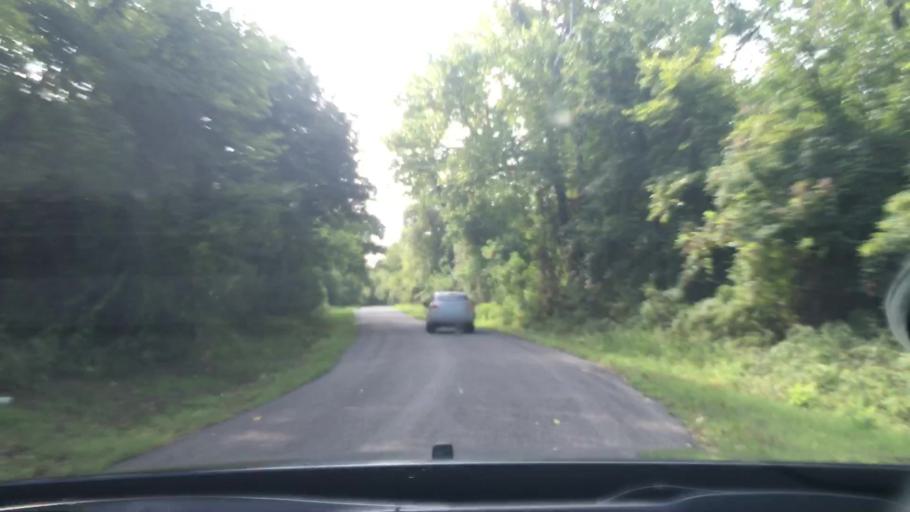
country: US
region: Oklahoma
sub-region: Johnston County
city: Tishomingo
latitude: 34.2032
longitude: -96.6689
